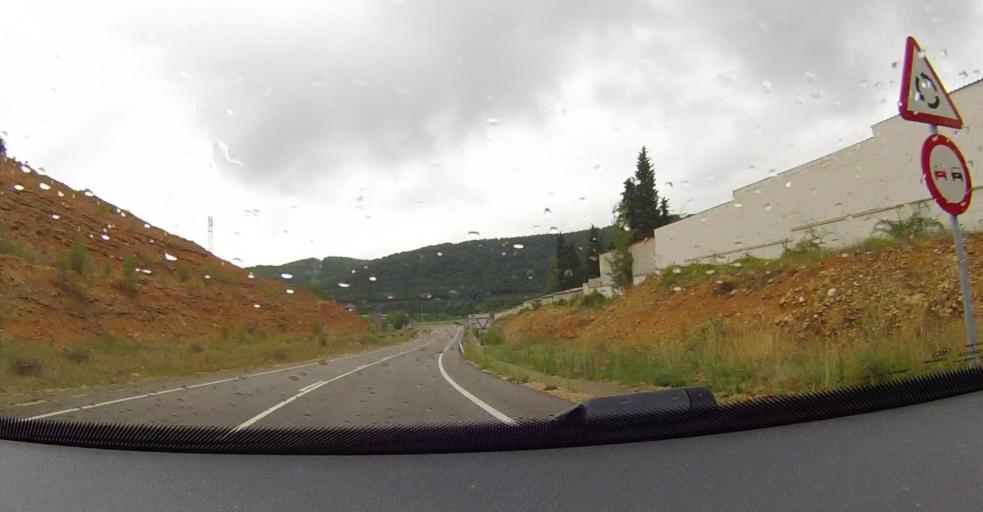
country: ES
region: Castille and Leon
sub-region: Provincia de Leon
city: Cistierna
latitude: 42.7953
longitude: -5.1240
